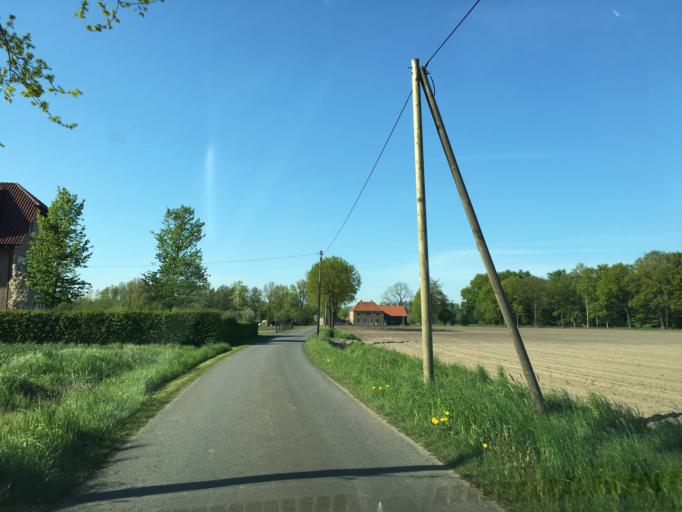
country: DE
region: North Rhine-Westphalia
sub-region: Regierungsbezirk Munster
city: Nordkirchen
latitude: 51.7541
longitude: 7.4921
